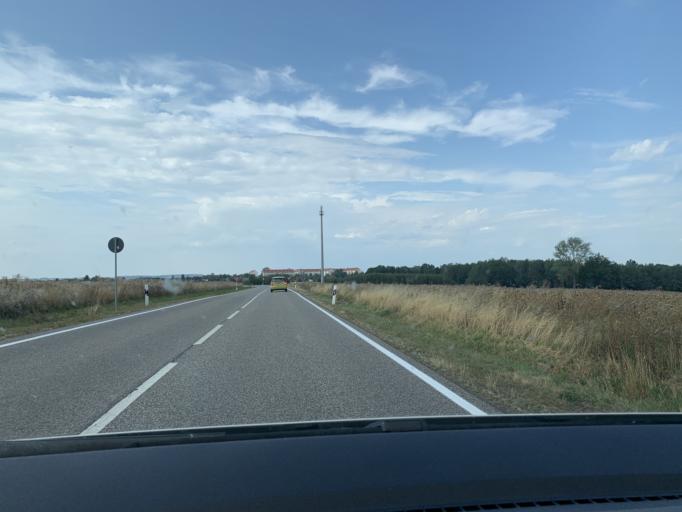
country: DE
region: Saxony
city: Frankenberg
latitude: 50.9091
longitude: 13.0701
